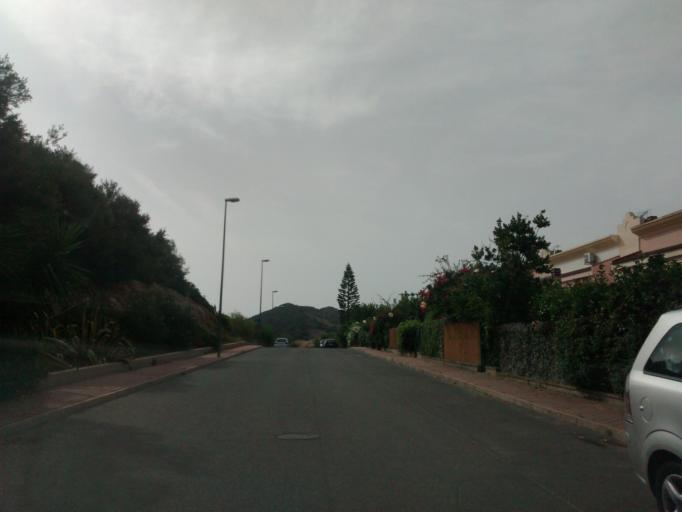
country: IT
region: Sardinia
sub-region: Provincia di Cagliari
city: Villasimius
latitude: 39.1506
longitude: 9.5205
